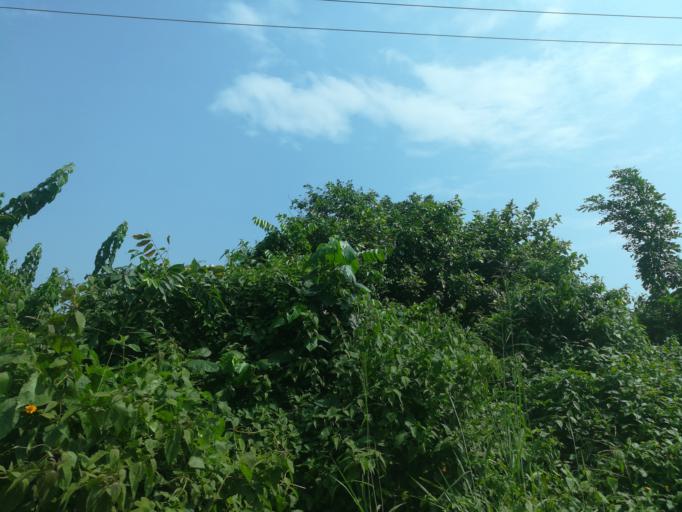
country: NG
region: Lagos
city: Ikorodu
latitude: 6.6006
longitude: 3.6254
